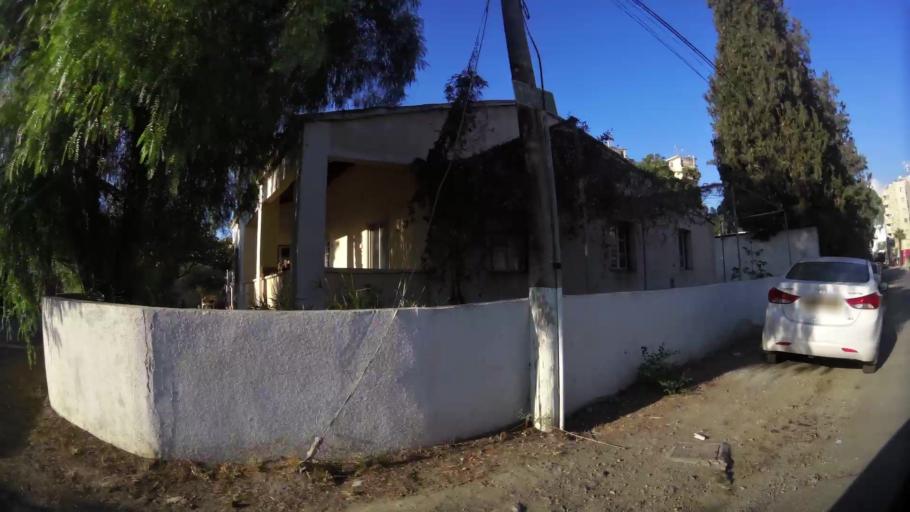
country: CY
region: Lefkosia
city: Nicosia
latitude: 35.1981
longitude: 33.3460
